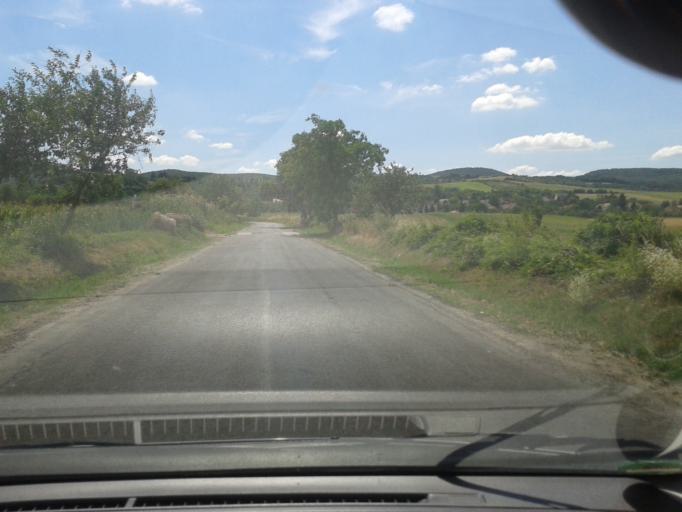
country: HU
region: Komarom-Esztergom
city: Pilismarot
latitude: 47.7908
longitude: 18.8779
